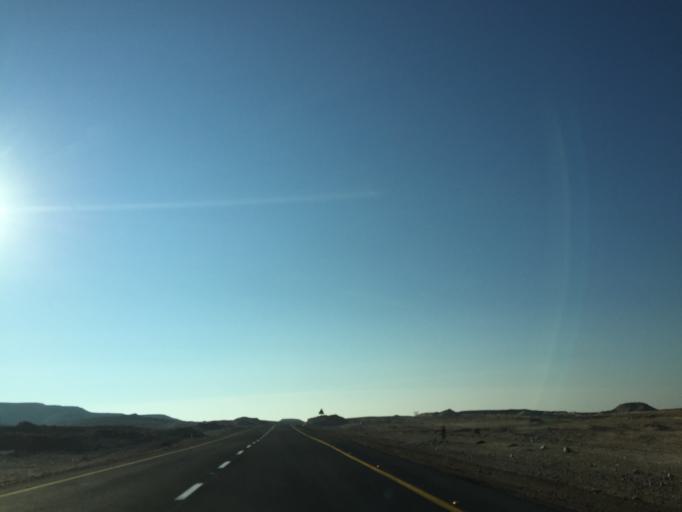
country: IL
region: Southern District
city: Mitzpe Ramon
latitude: 30.2701
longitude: 35.0222
